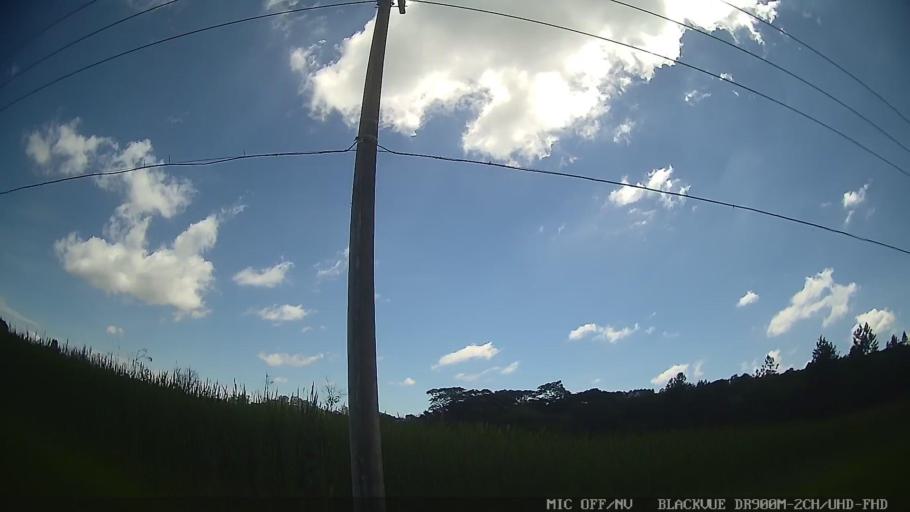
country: BR
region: Sao Paulo
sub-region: Mogi das Cruzes
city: Mogi das Cruzes
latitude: -23.6347
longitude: -46.2025
